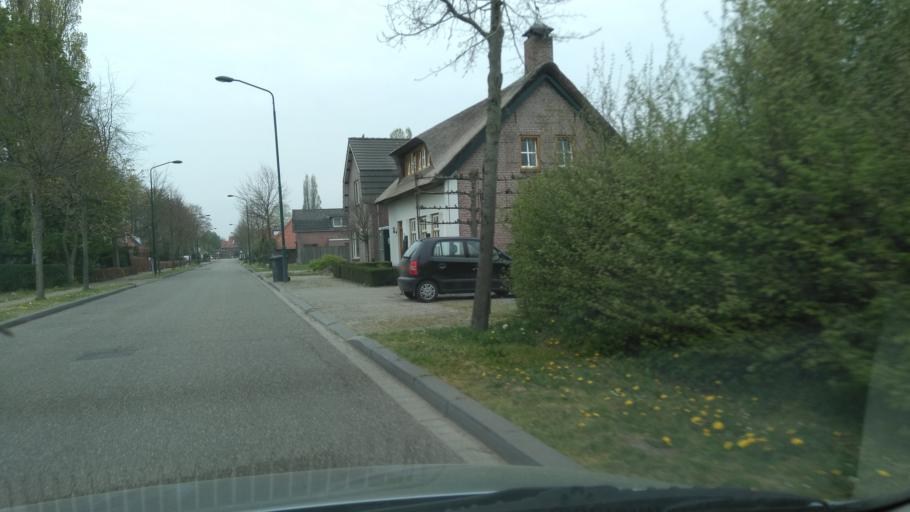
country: NL
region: North Brabant
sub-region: Gemeente Baarle-Nassau
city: Baarle-Nassau
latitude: 51.4775
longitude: 4.9633
